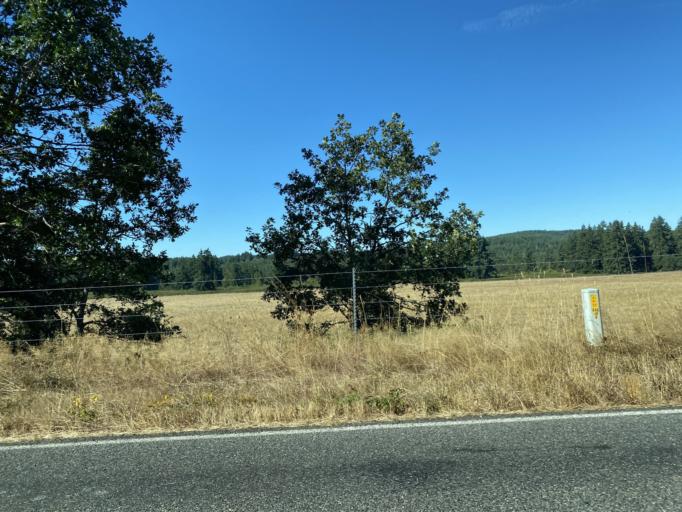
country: US
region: Washington
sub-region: Thurston County
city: Rainier
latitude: 46.8925
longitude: -122.7519
